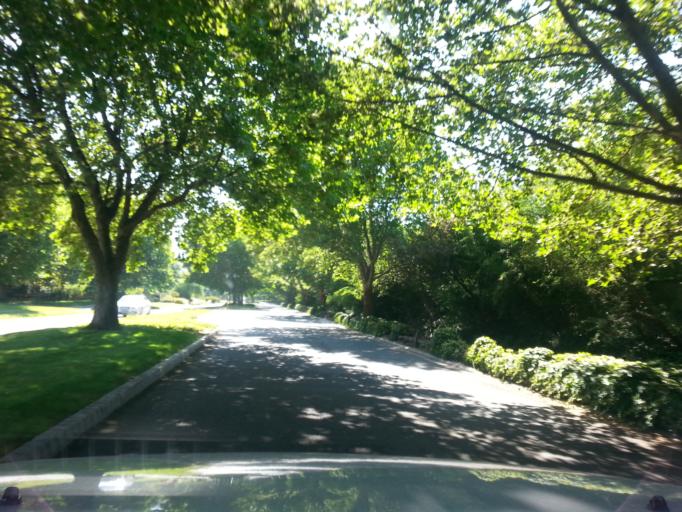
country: CL
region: Santiago Metropolitan
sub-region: Provincia de Chacabuco
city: Chicureo Abajo
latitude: -33.2425
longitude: -70.6903
